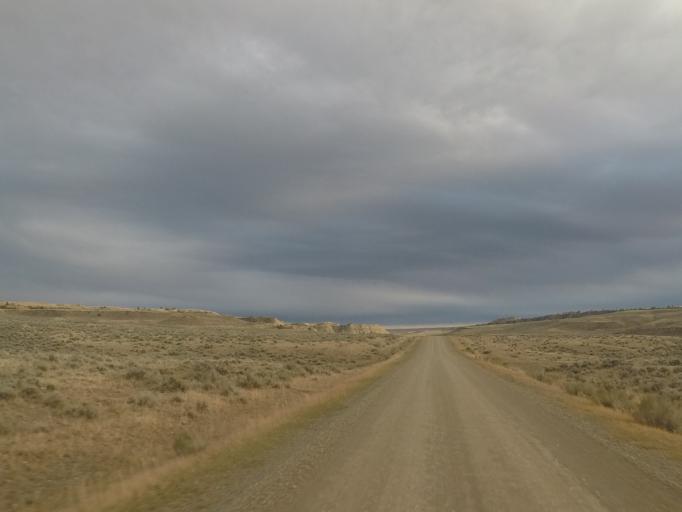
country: US
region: Montana
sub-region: Golden Valley County
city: Ryegate
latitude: 46.4556
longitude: -109.2634
